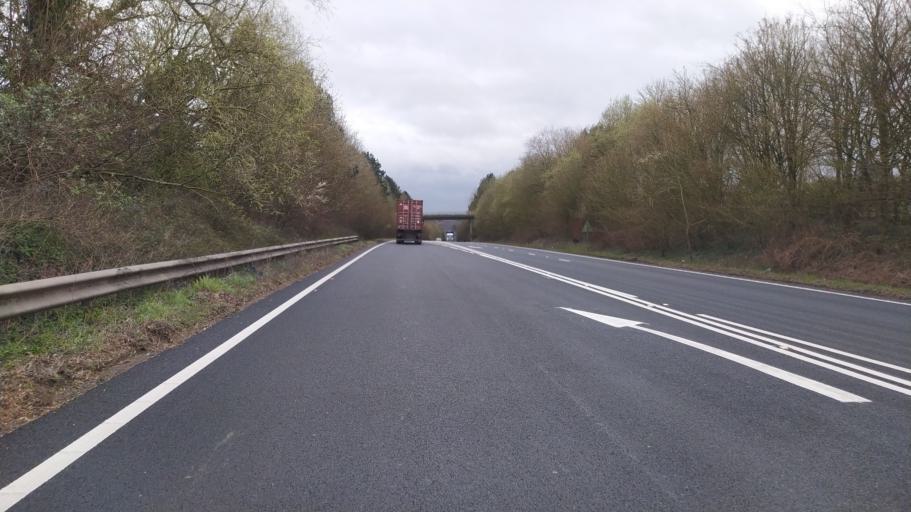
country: GB
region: England
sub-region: Wiltshire
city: Warminster
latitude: 51.1947
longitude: -2.1986
